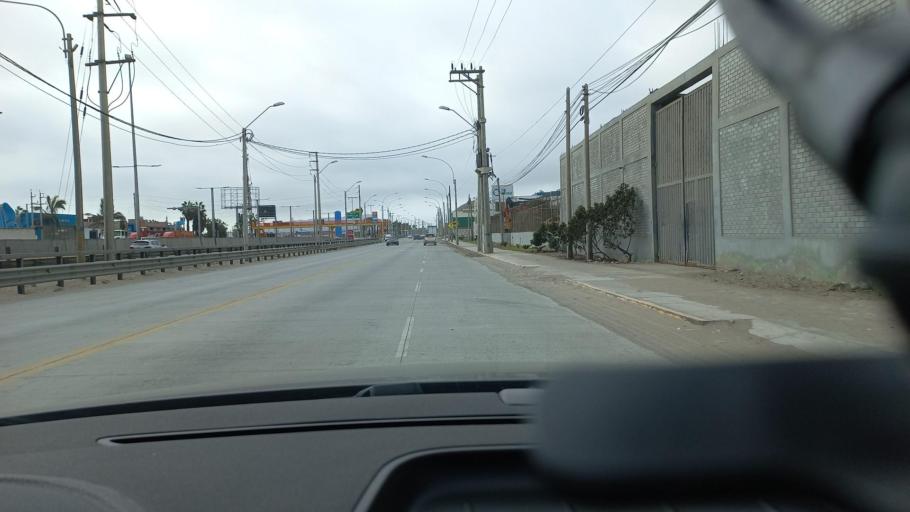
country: PE
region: Lima
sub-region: Lima
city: Surco
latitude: -12.2266
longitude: -76.9701
